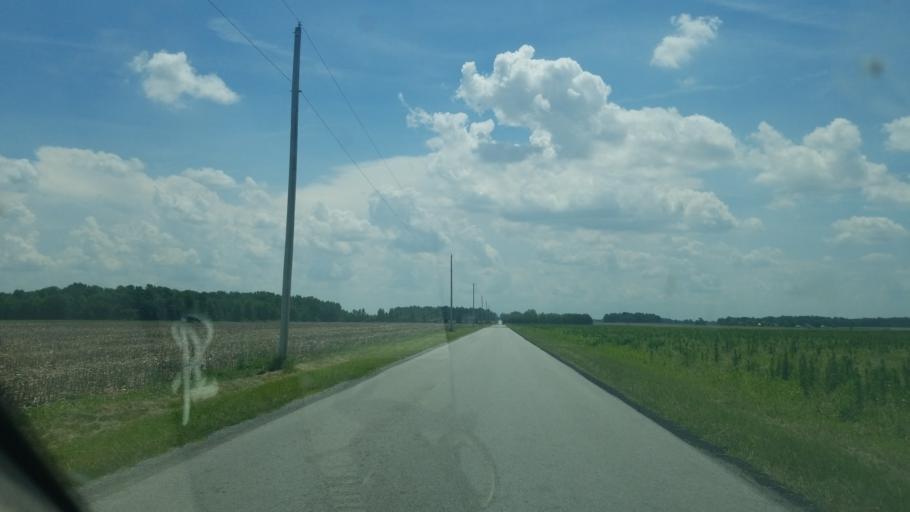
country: US
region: Ohio
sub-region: Hancock County
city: Arlington
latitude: 40.8909
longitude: -83.5996
